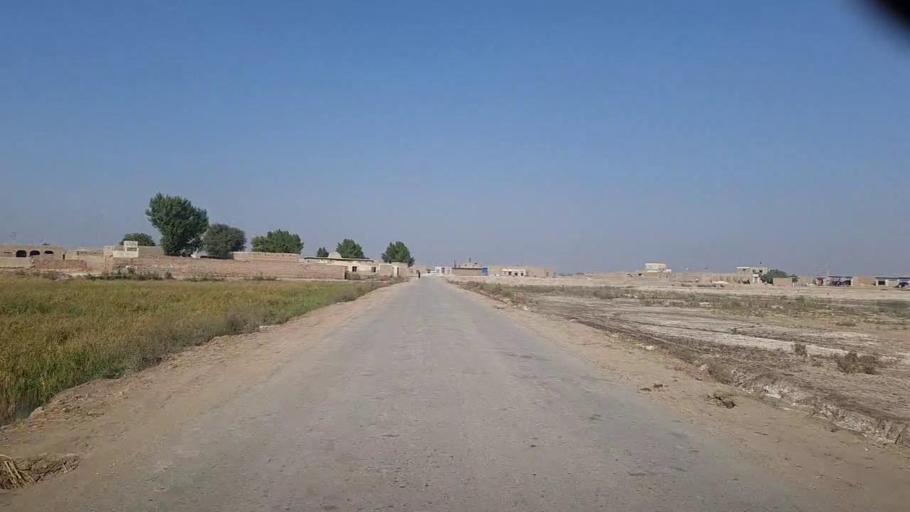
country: PK
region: Sindh
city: Tangwani
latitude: 28.2608
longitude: 68.9992
